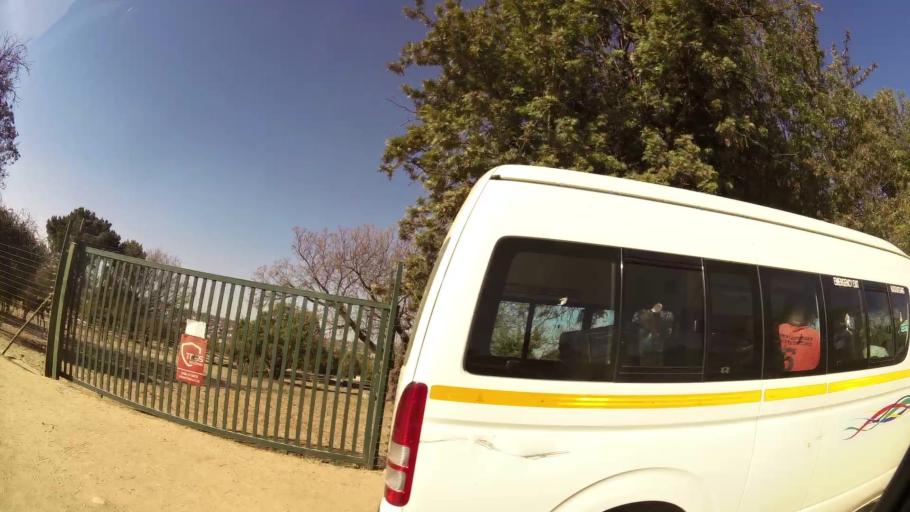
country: ZA
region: Gauteng
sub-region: City of Johannesburg Metropolitan Municipality
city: Diepsloot
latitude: -26.0119
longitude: 27.9663
